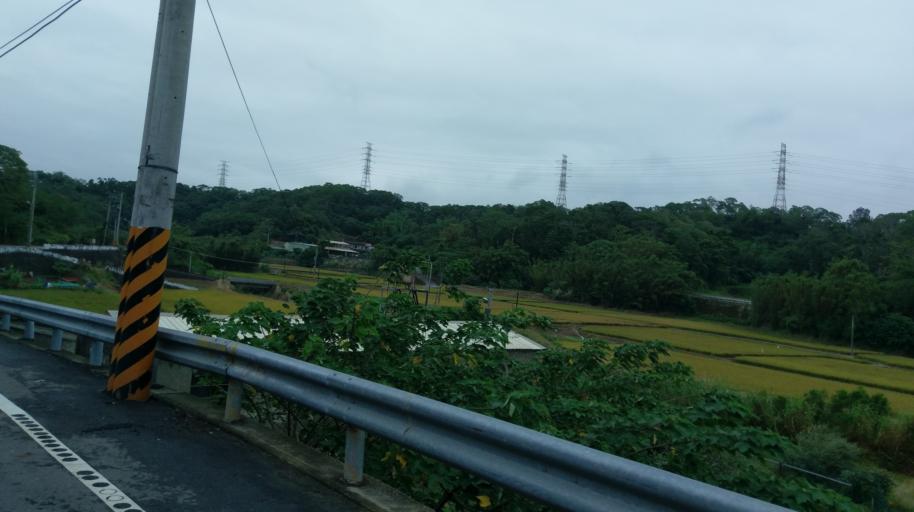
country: TW
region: Taiwan
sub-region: Hsinchu
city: Hsinchu
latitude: 24.7337
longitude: 120.9458
